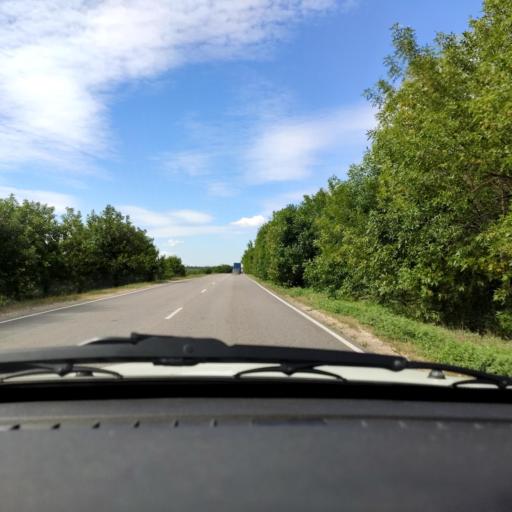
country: RU
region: Voronezj
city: Volya
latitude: 51.7076
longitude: 39.5250
